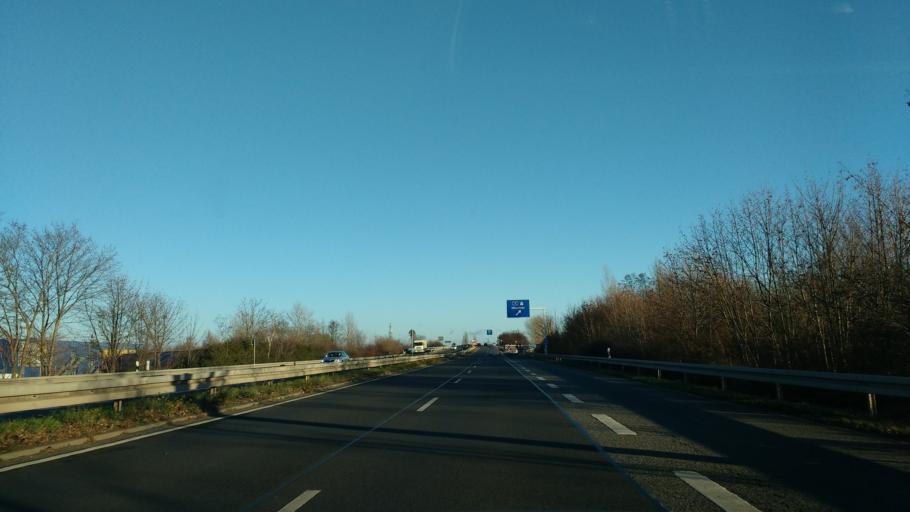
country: DE
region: Saxony-Anhalt
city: Gunthersdorf
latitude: 51.3468
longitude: 12.1802
